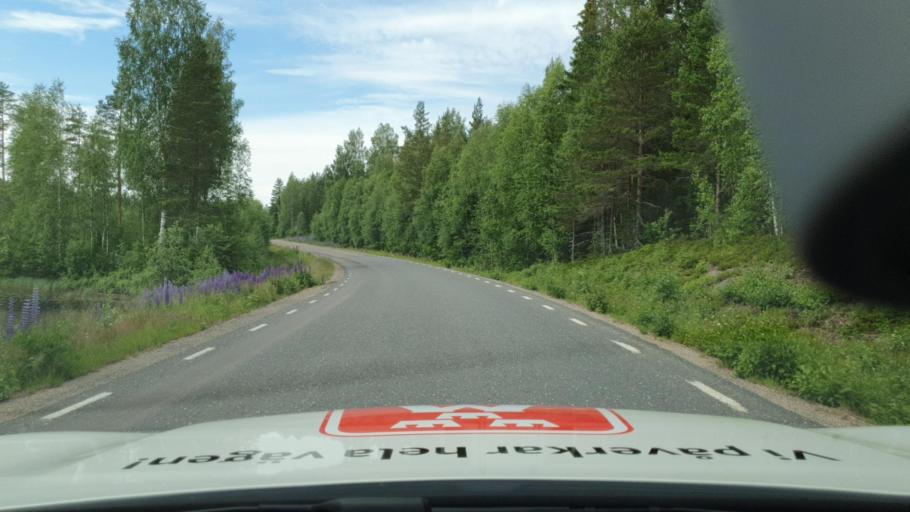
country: NO
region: Hedmark
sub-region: Grue
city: Kirkenaer
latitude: 60.6816
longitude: 12.6552
